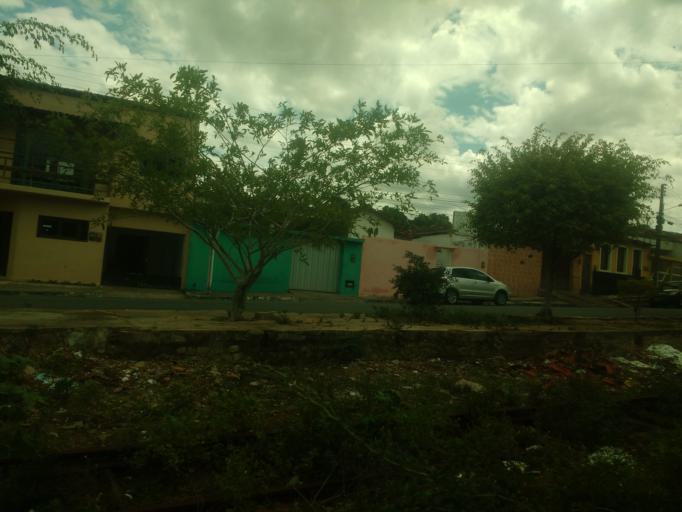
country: BR
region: Alagoas
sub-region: Uniao Dos Palmares
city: Uniao dos Palmares
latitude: -9.1616
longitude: -36.0307
